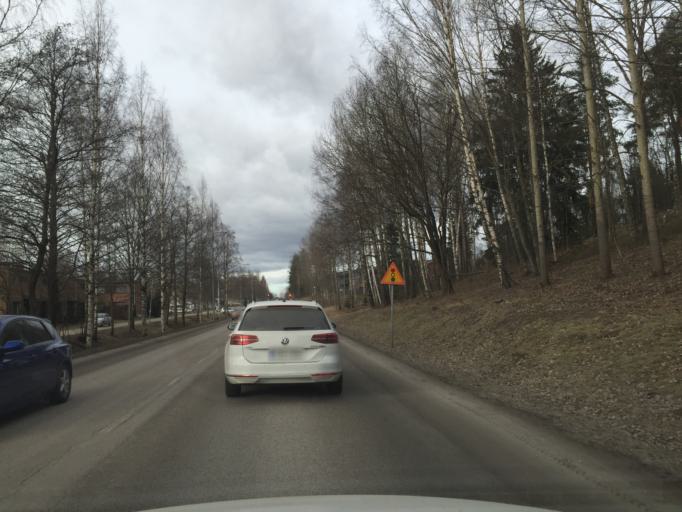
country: FI
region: Uusimaa
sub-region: Helsinki
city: Teekkarikylae
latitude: 60.2811
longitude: 24.8727
